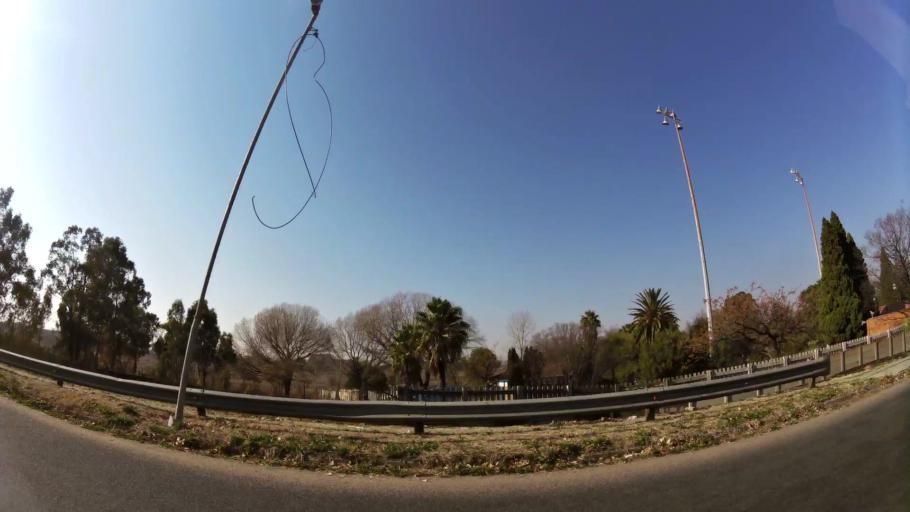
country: ZA
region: Gauteng
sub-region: Ekurhuleni Metropolitan Municipality
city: Boksburg
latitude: -26.2286
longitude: 28.2366
